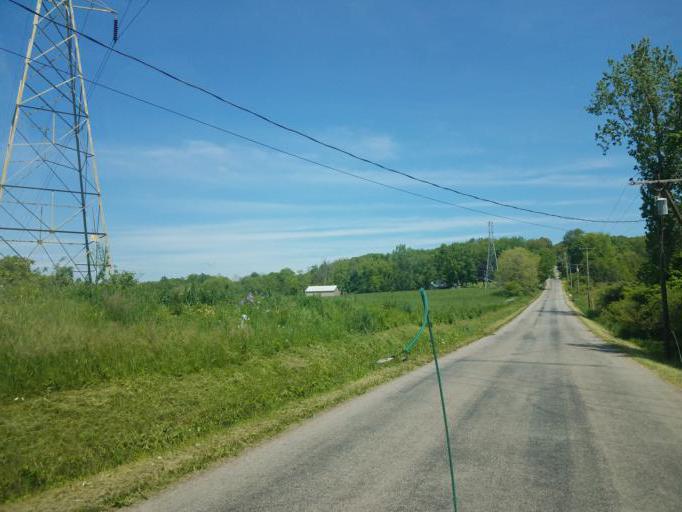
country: US
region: Ohio
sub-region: Ashland County
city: Ashland
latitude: 40.8647
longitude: -82.2501
